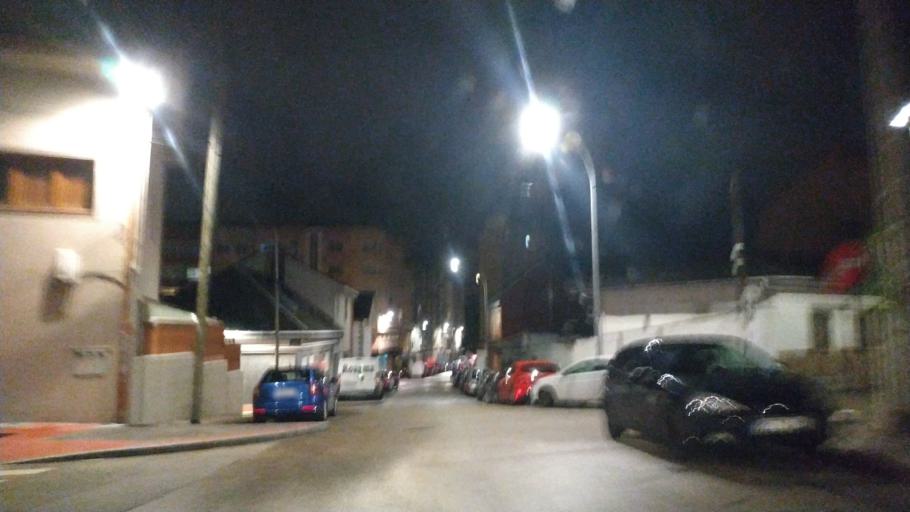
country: ES
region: Galicia
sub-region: Provincia da Coruna
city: A Coruna
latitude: 43.3590
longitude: -8.4145
